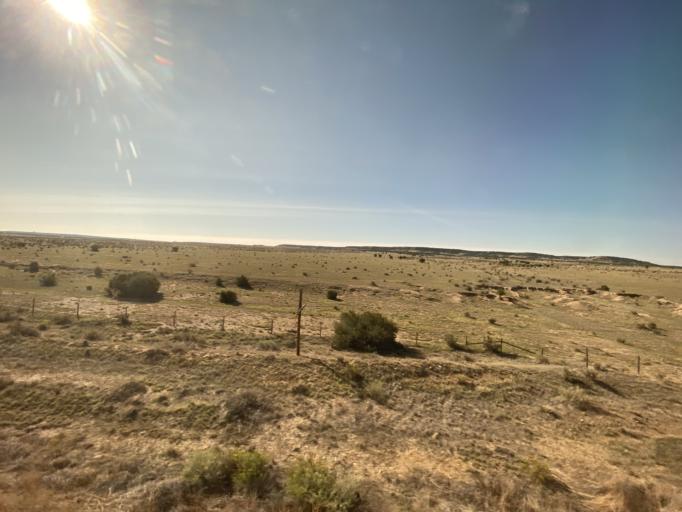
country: US
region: Colorado
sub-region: Otero County
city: Fowler
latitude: 37.5657
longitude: -104.0767
